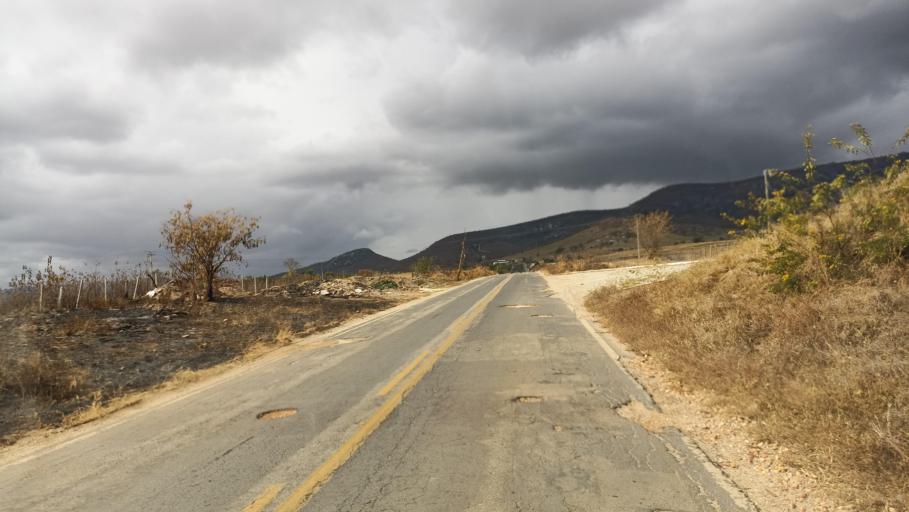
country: BR
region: Minas Gerais
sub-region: Itinga
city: Itinga
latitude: -16.6213
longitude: -41.7729
